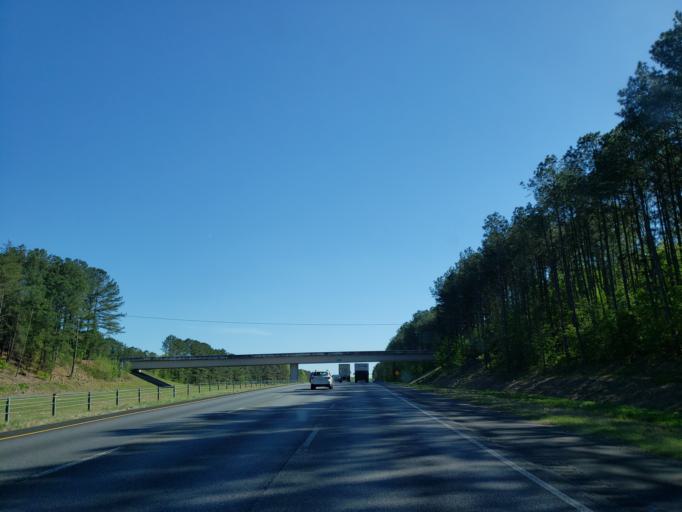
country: US
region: Georgia
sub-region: Cherokee County
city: Canton
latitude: 34.2126
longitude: -84.4917
